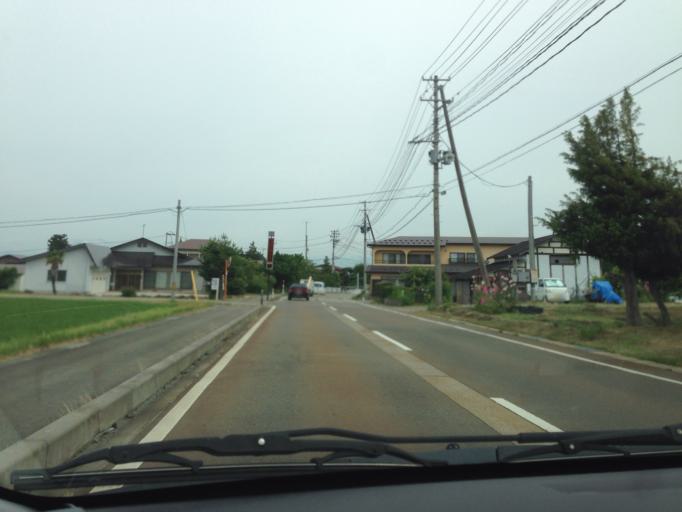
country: JP
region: Fukushima
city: Kitakata
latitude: 37.5793
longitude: 139.9135
